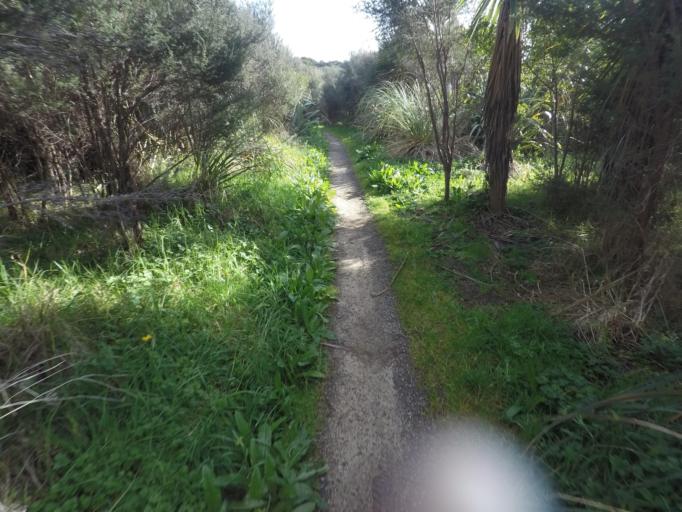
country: NZ
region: Auckland
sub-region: Auckland
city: Manukau City
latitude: -36.9989
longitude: 174.9108
